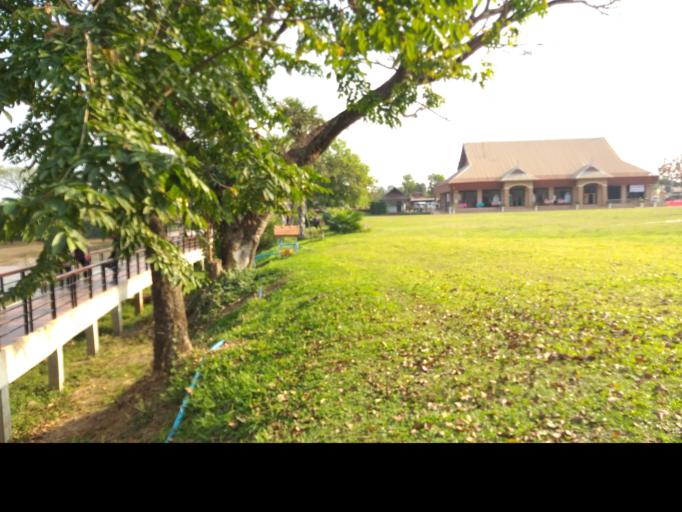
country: TH
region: Changwat Udon Thani
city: Ban Dung
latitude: 17.7436
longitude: 103.3598
